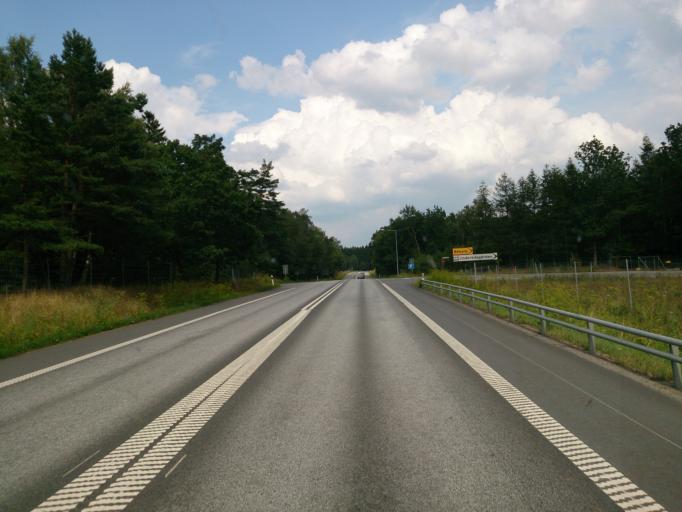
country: SE
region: Skane
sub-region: Horby Kommun
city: Hoerby
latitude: 55.9242
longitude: 13.7923
